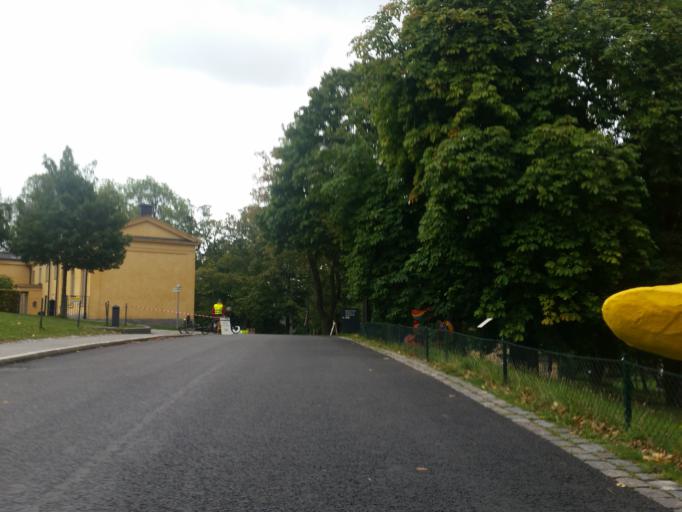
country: SE
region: Stockholm
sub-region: Stockholms Kommun
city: OEstermalm
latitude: 59.3252
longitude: 18.0833
